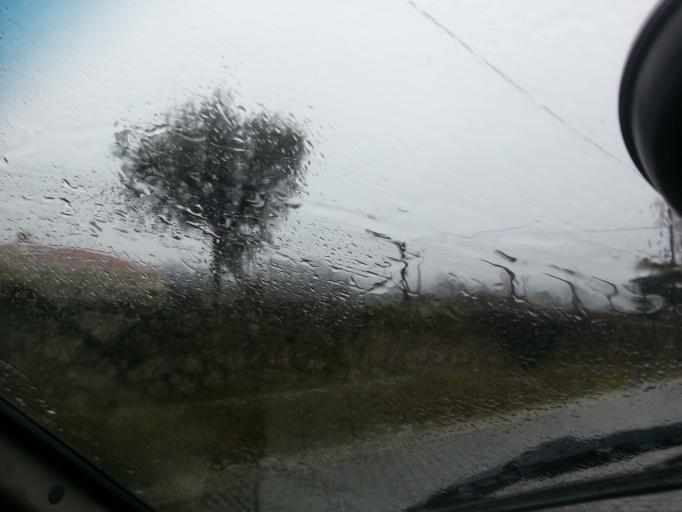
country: PT
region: Guarda
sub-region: Fornos de Algodres
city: Fornos de Algodres
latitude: 40.6079
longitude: -7.6430
